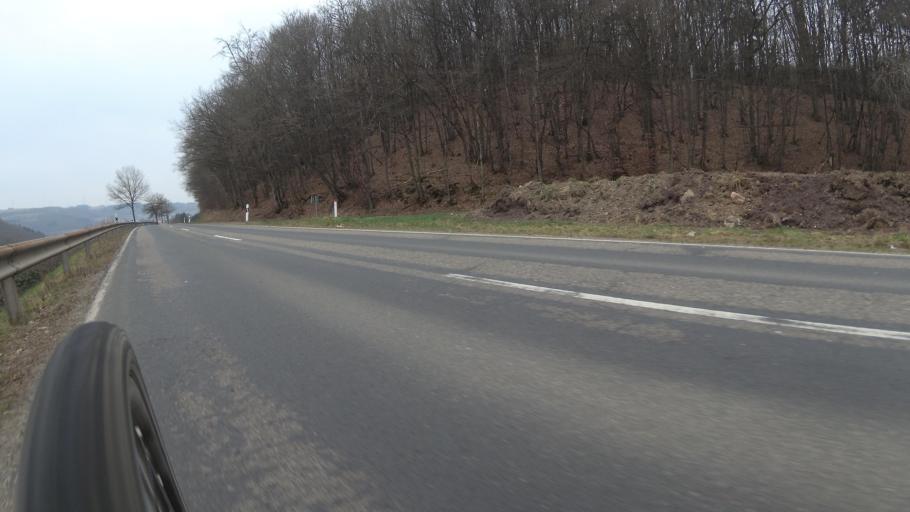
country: DE
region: Rheinland-Pfalz
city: Dienstweiler
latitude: 49.6305
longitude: 7.1933
